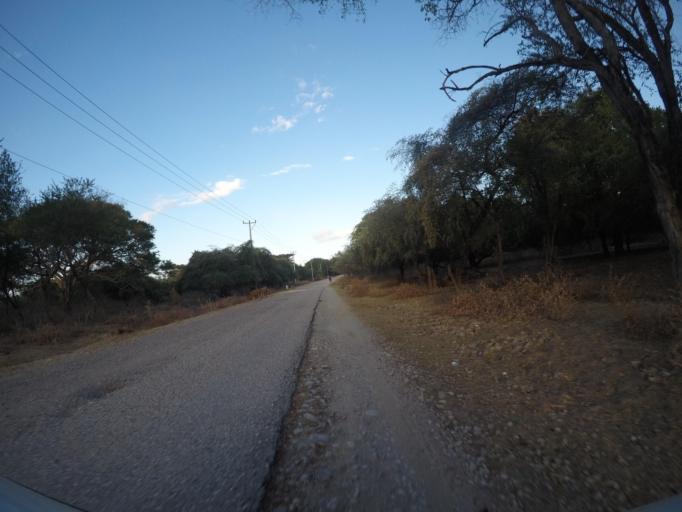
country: TL
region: Lautem
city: Lospalos
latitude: -8.3266
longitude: 126.9934
